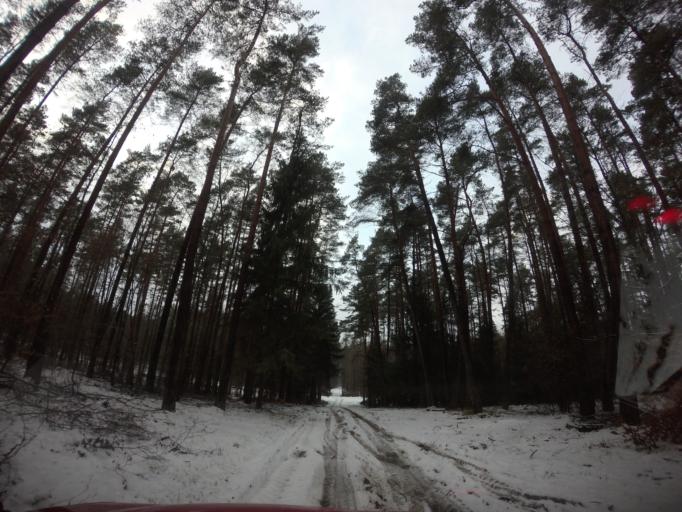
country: PL
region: West Pomeranian Voivodeship
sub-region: Powiat choszczenski
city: Pelczyce
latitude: 52.9553
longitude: 15.3532
